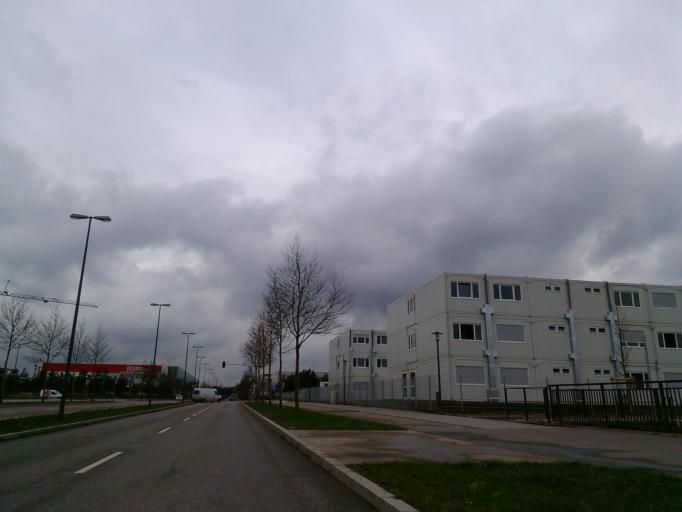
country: DE
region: Bavaria
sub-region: Upper Bavaria
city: Grafelfing
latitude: 48.1376
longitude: 11.4094
